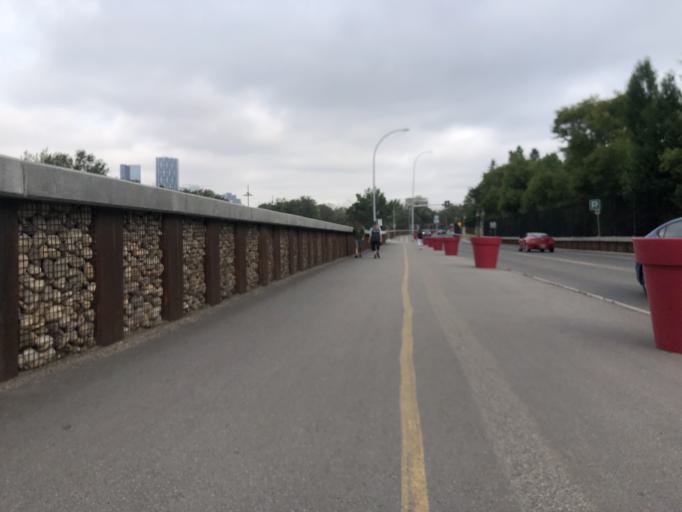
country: CA
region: Alberta
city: Calgary
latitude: 51.0454
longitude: -114.0342
